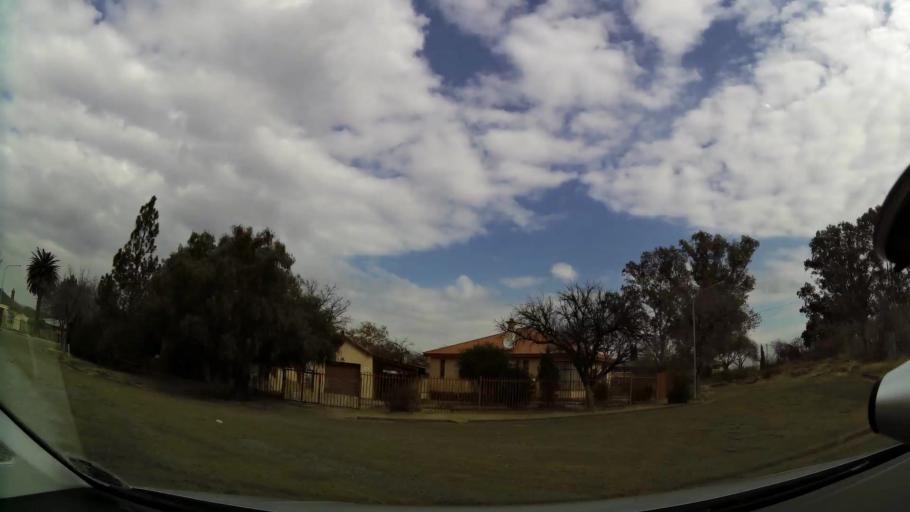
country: ZA
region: Orange Free State
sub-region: Fezile Dabi District Municipality
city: Kroonstad
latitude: -27.6536
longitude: 27.2339
